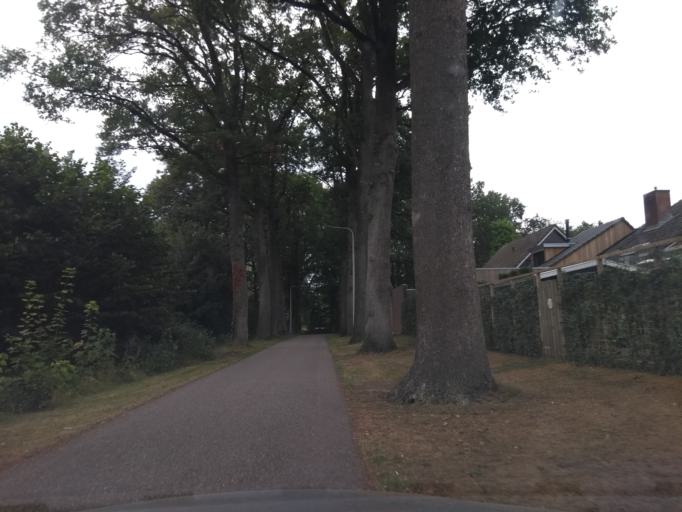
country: NL
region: Overijssel
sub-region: Gemeente Oldenzaal
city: Oldenzaal
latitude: 52.3733
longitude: 6.9967
